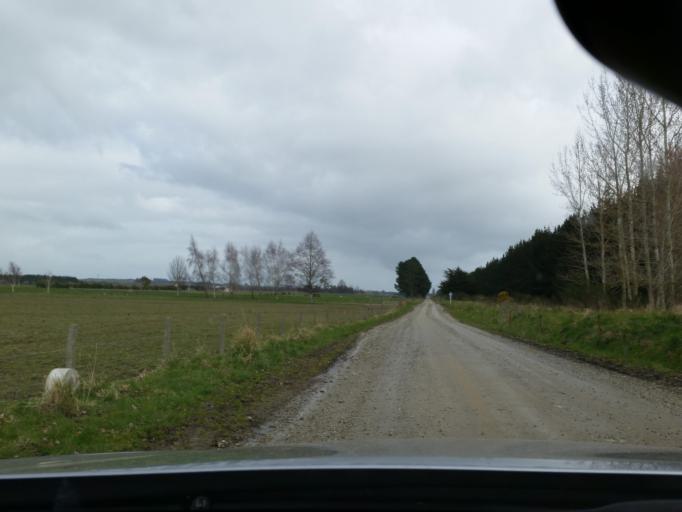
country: NZ
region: Southland
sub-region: Southland District
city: Winton
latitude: -46.2141
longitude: 168.4992
